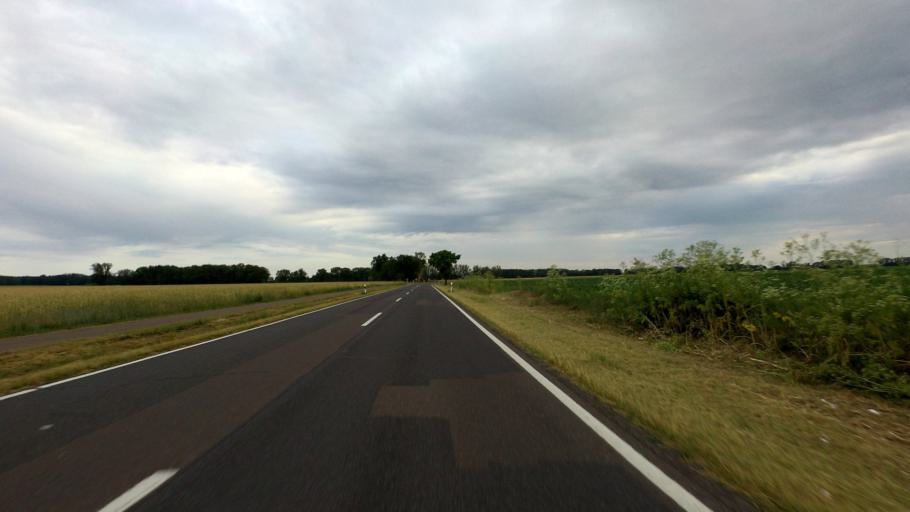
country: DE
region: Brandenburg
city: Pawesin
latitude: 52.4971
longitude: 12.7054
